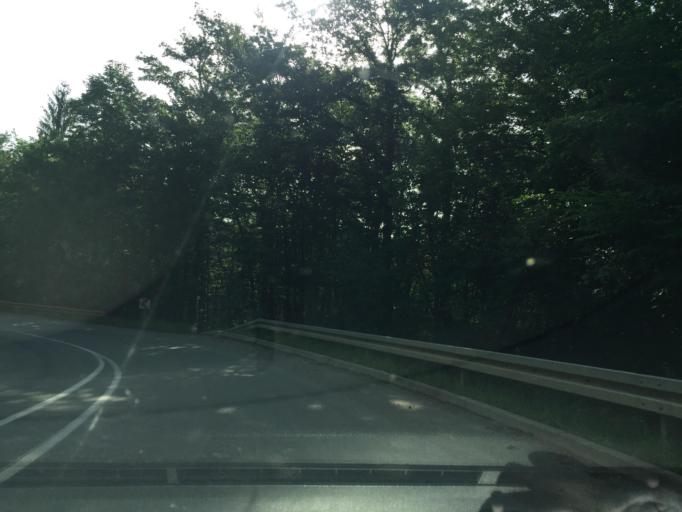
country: HR
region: Primorsko-Goranska
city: Kastav
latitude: 45.4218
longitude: 14.3237
